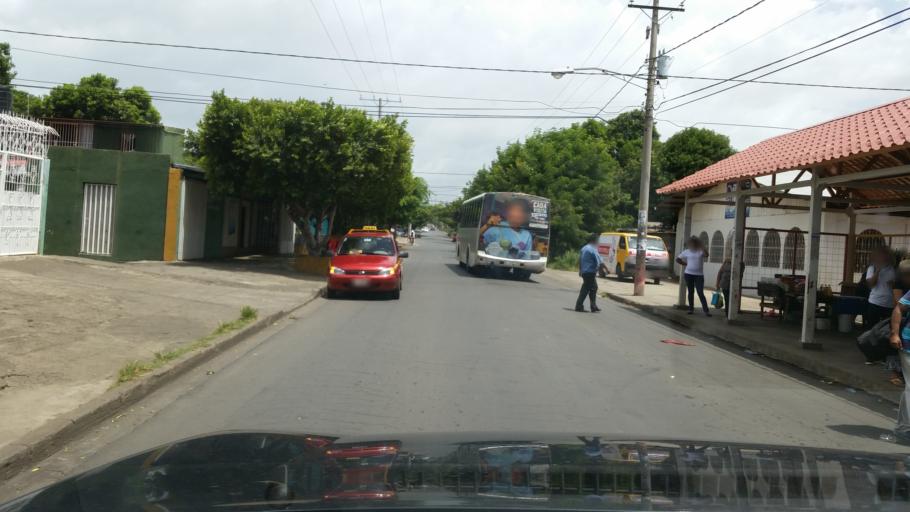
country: NI
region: Managua
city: Managua
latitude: 12.1274
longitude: -86.2150
